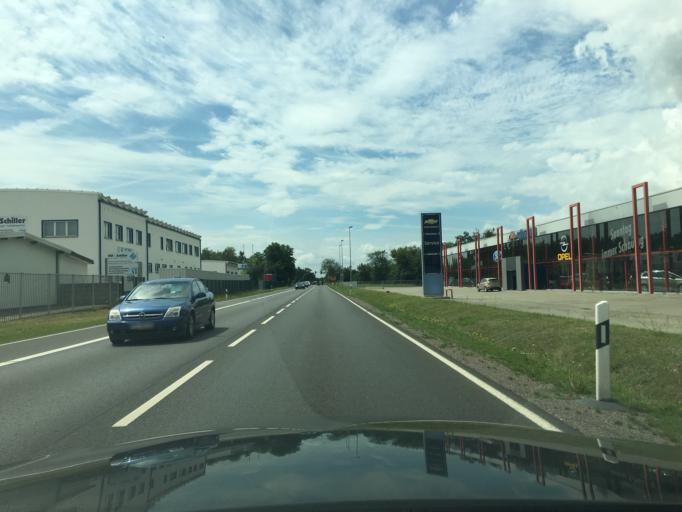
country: DE
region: Saxony-Anhalt
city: Zscherndorf
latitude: 51.6000
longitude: 12.2838
